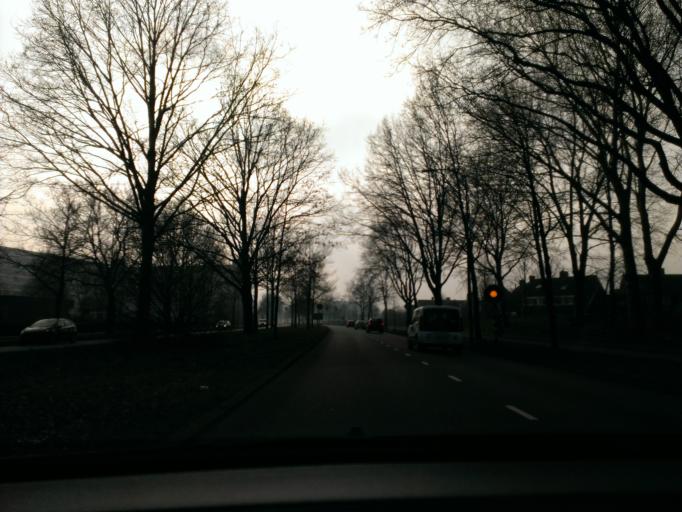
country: NL
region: Overijssel
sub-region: Gemeente Zwolle
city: Zwolle
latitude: 52.5297
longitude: 6.1095
